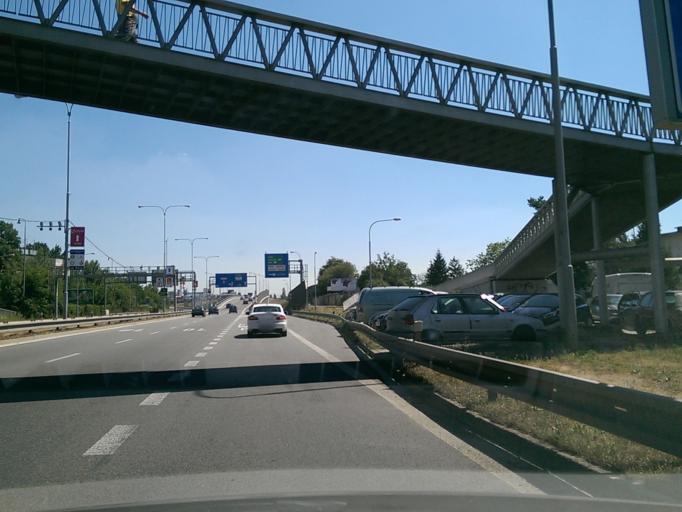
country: CZ
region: South Moravian
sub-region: Mesto Brno
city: Brno
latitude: 49.2246
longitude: 16.6004
